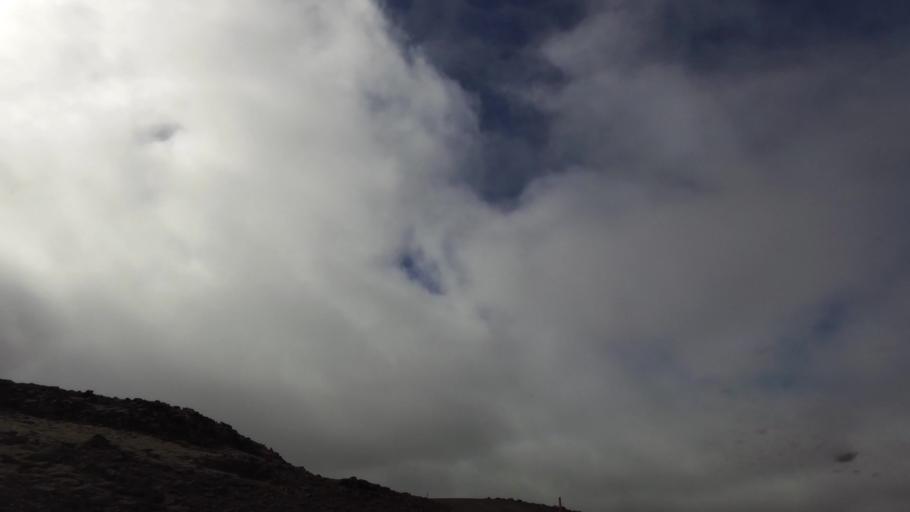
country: IS
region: West
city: Olafsvik
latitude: 65.5442
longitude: -24.3150
